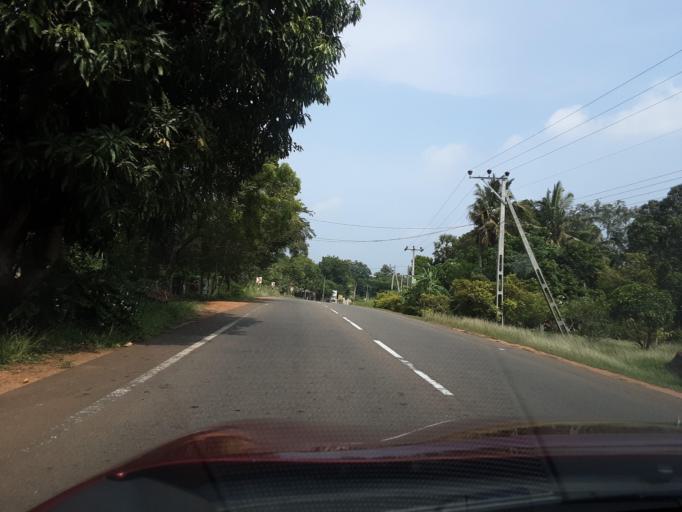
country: LK
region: North Central
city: Anuradhapura
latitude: 8.3342
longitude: 80.5011
